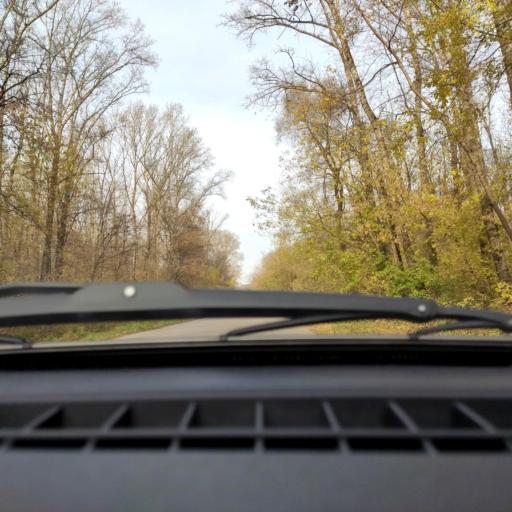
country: RU
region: Bashkortostan
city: Ufa
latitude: 54.7942
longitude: 56.1548
